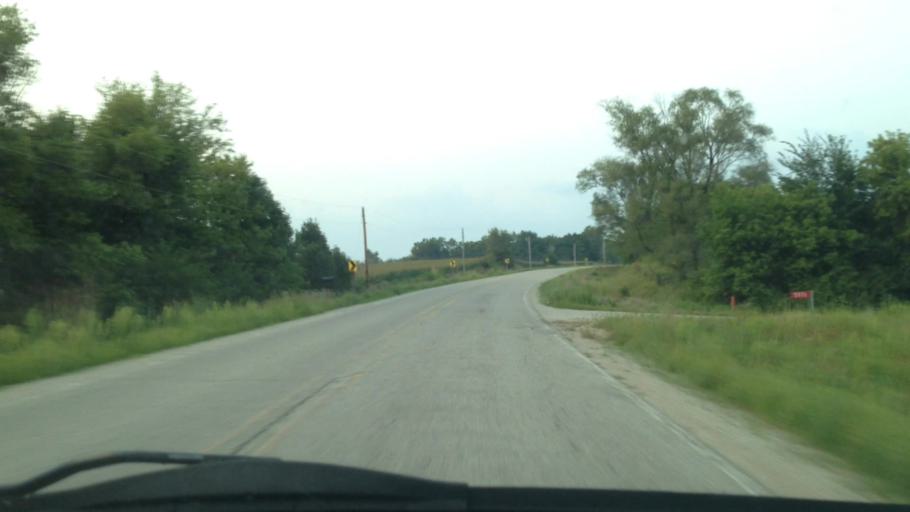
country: US
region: Iowa
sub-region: Benton County
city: Urbana
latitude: 42.1562
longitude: -91.8774
